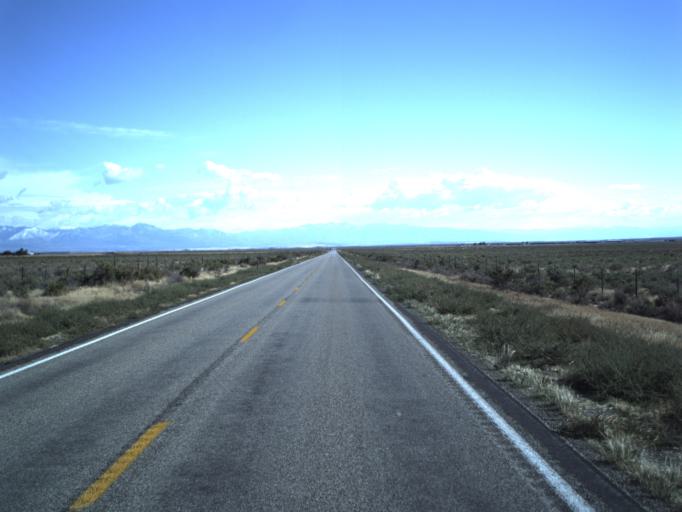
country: US
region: Utah
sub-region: Millard County
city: Delta
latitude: 39.3444
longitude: -112.4941
